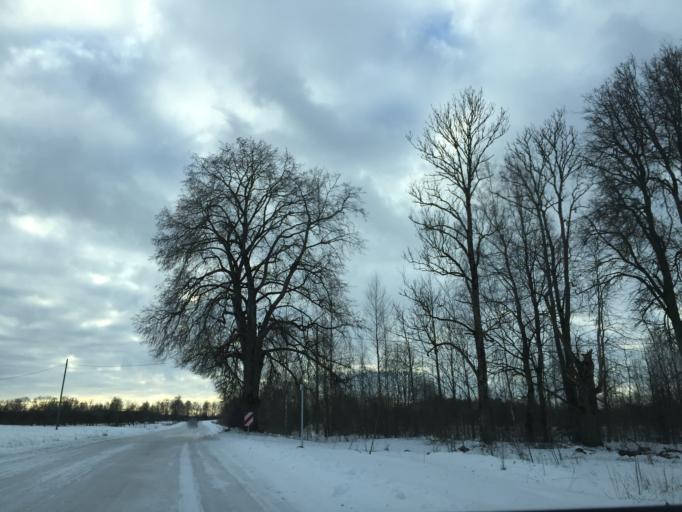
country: LV
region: Lielvarde
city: Lielvarde
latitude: 56.5718
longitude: 24.7341
